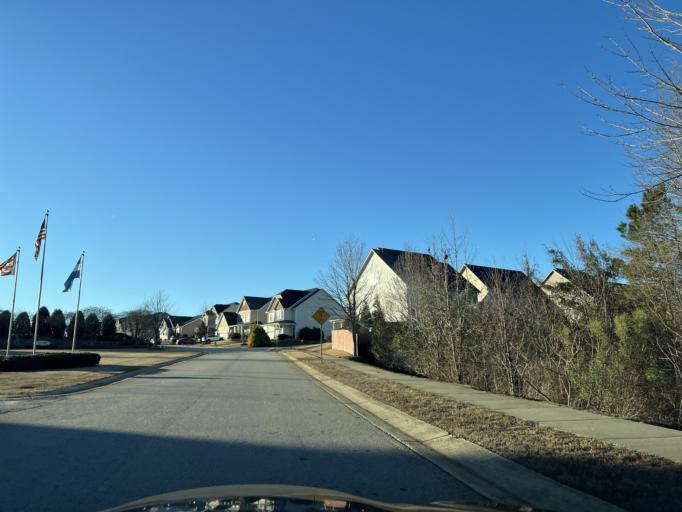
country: US
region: North Carolina
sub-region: Wake County
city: Fuquay-Varina
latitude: 35.5742
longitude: -78.8113
